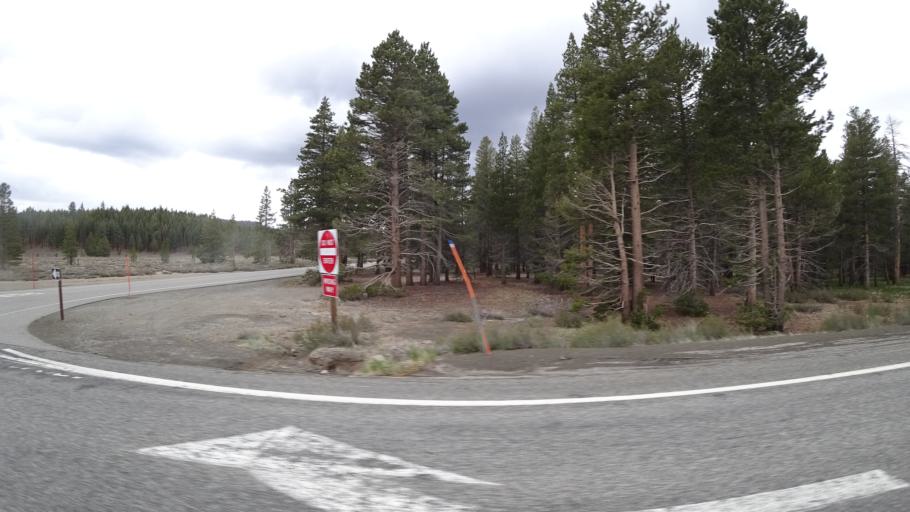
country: US
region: California
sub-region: Mono County
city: Mammoth Lakes
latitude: 37.7097
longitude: -118.9532
